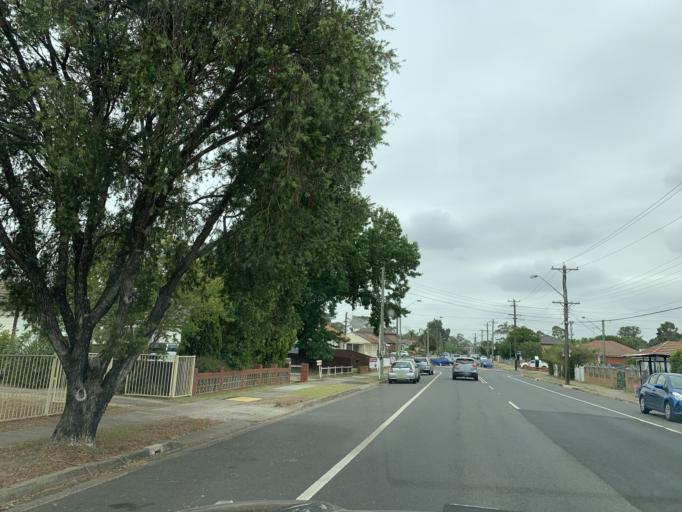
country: AU
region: New South Wales
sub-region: Blacktown
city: Doonside
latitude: -33.7591
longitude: 150.8702
